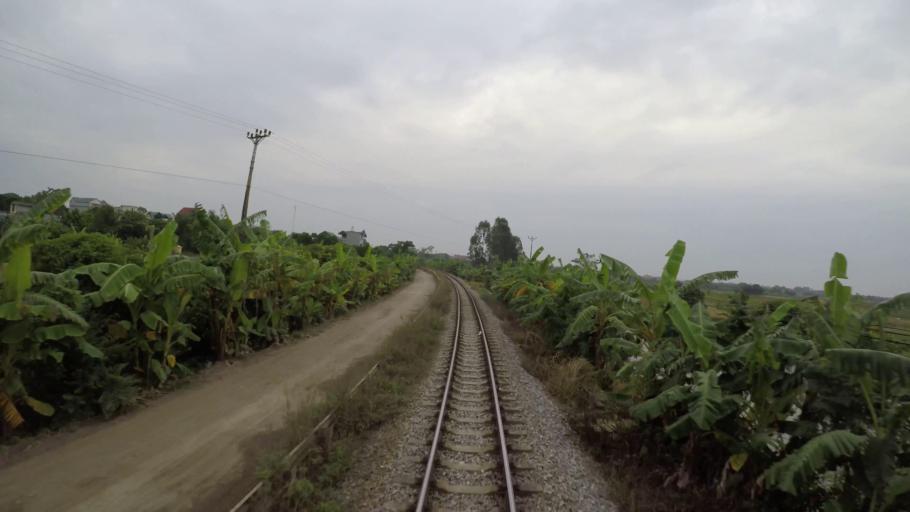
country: VN
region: Hai Duong
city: Ke Sat
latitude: 20.9659
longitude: 106.1353
